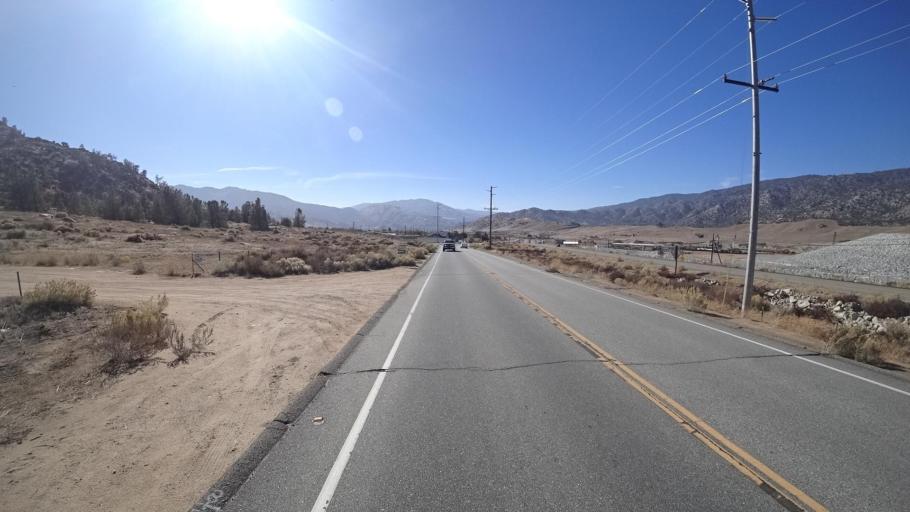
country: US
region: California
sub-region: Kern County
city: Lake Isabella
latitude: 35.6401
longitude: -118.4632
